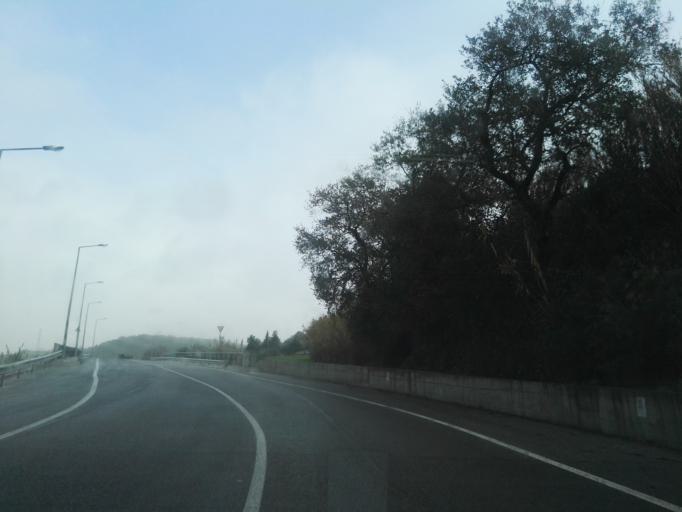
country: PT
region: Lisbon
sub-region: Vila Franca de Xira
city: Sobralinho
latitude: 38.9313
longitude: -9.0604
